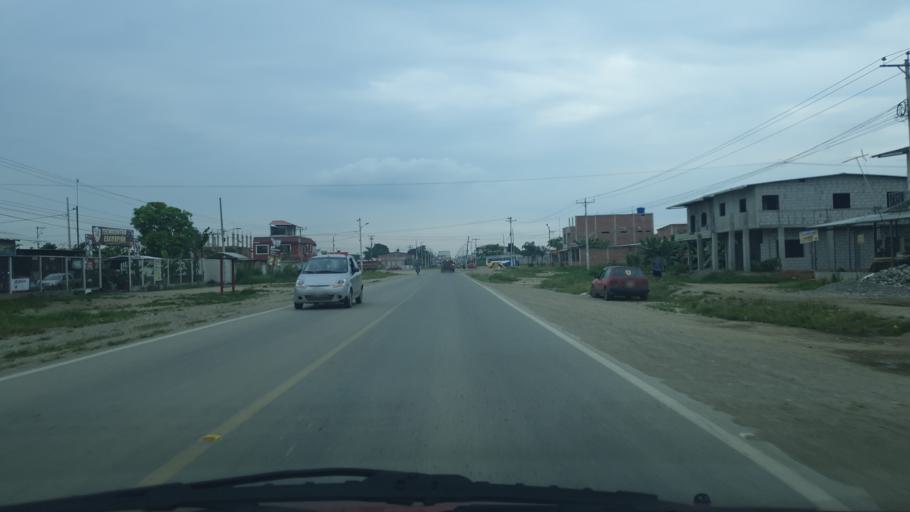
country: EC
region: El Oro
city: Pasaje
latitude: -3.3432
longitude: -79.8145
